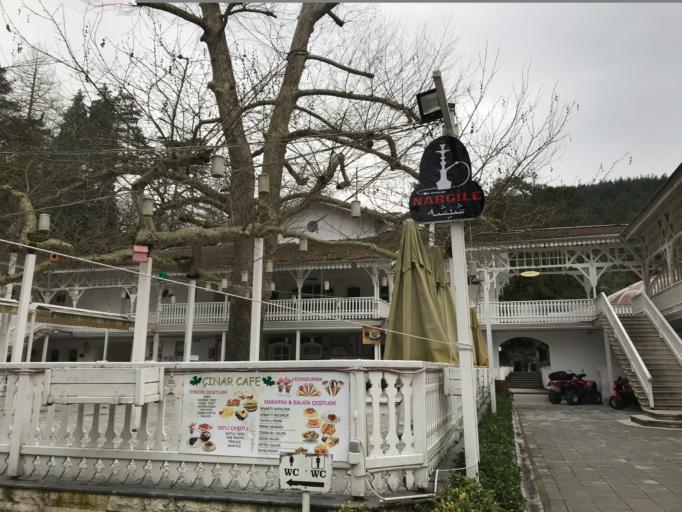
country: TR
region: Yalova
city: Termal
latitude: 40.6037
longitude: 29.1726
